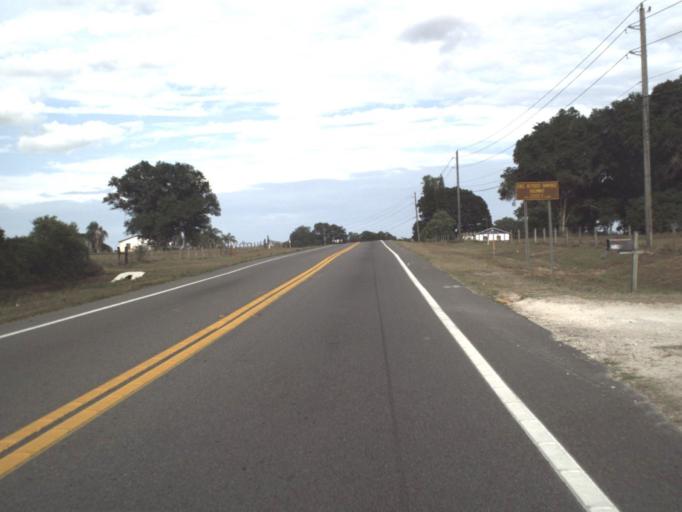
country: US
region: Florida
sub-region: Lake County
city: Mascotte
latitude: 28.5776
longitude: -81.9114
